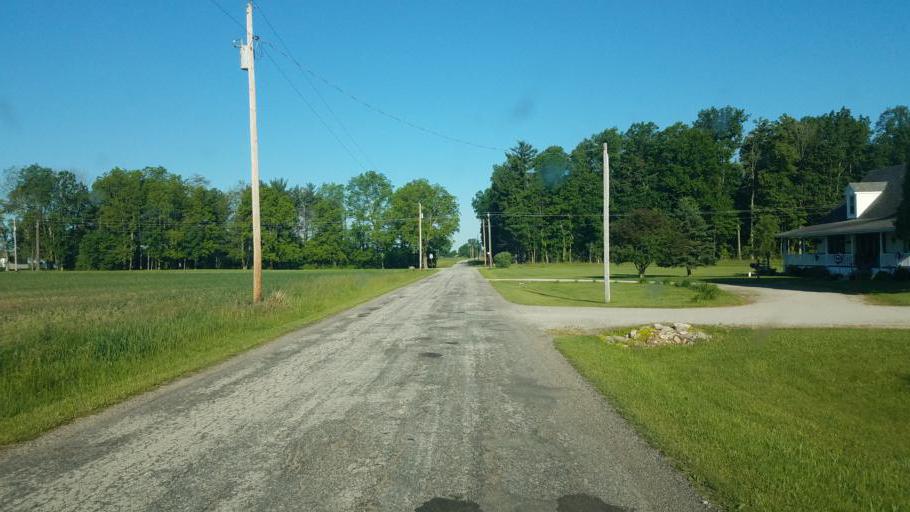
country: US
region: Ohio
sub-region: Morrow County
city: Cardington
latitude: 40.6162
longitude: -82.9510
